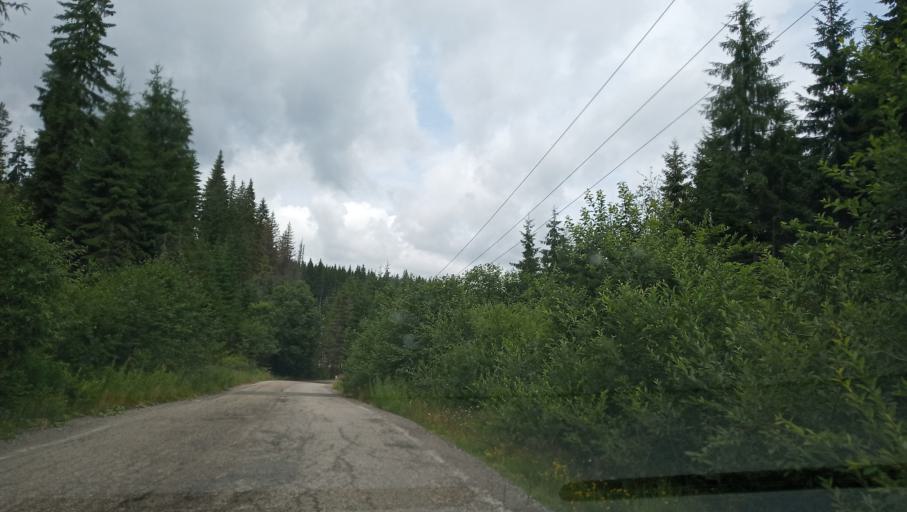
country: RO
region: Gorj
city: Novaci-Straini
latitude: 45.4165
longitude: 23.7089
